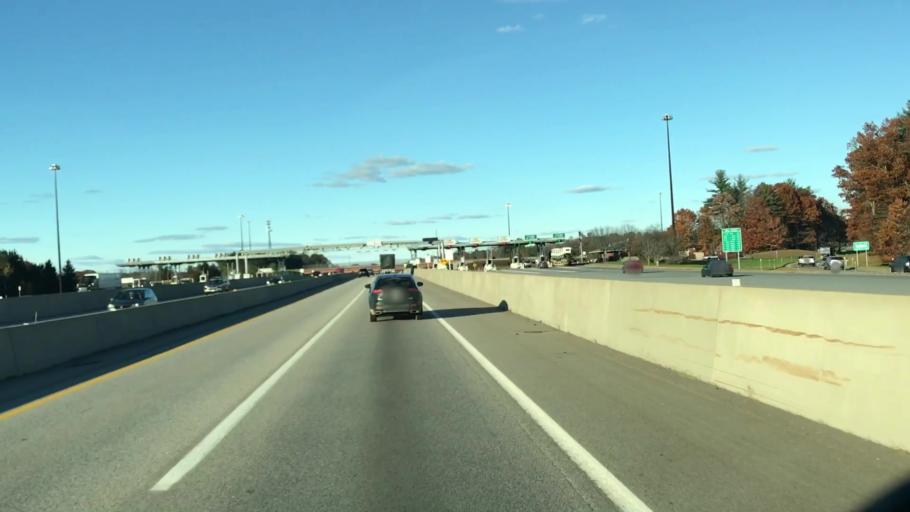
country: US
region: New Hampshire
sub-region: Rockingham County
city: Hampton
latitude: 42.9609
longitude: -70.8565
